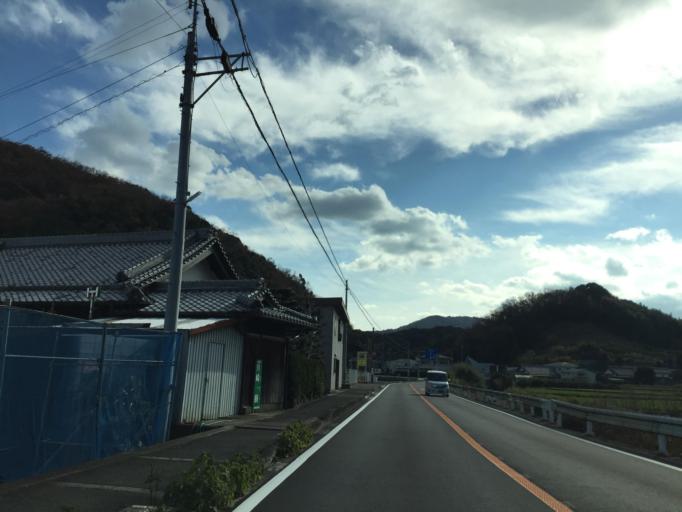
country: JP
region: Wakayama
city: Kainan
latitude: 34.1677
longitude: 135.2505
